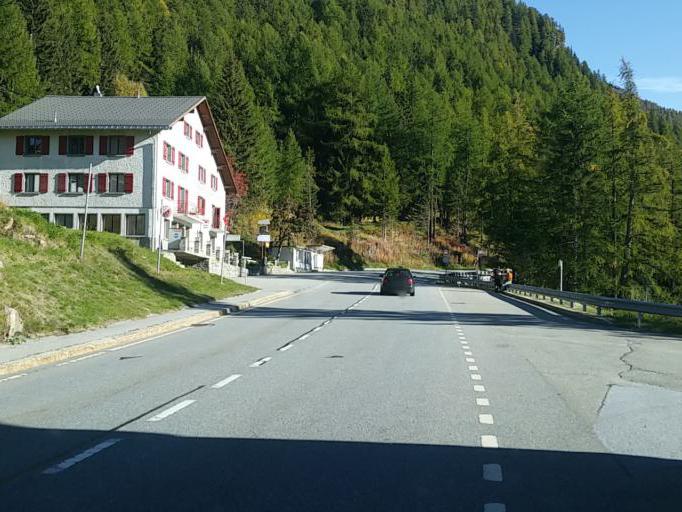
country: CH
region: Valais
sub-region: Brig District
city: Brig
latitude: 46.2801
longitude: 8.0371
